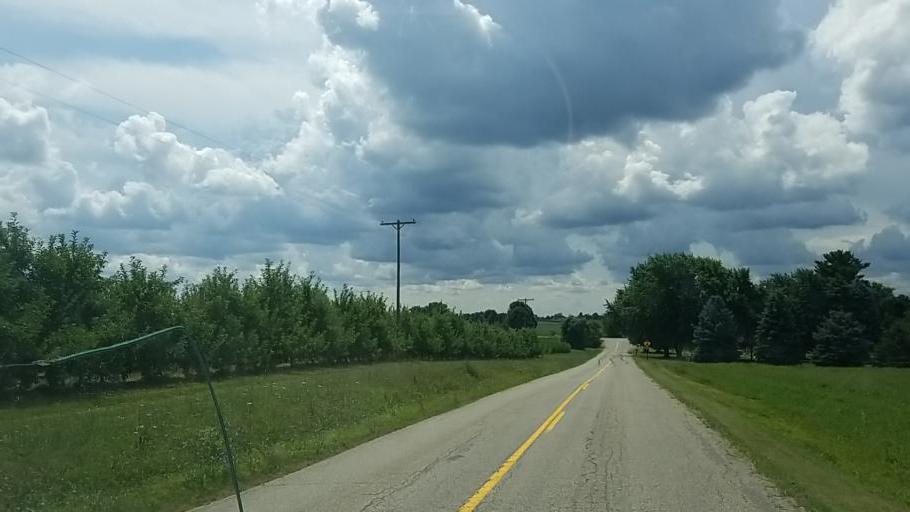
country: US
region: Michigan
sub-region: Kent County
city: Walker
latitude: 43.0620
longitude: -85.7487
